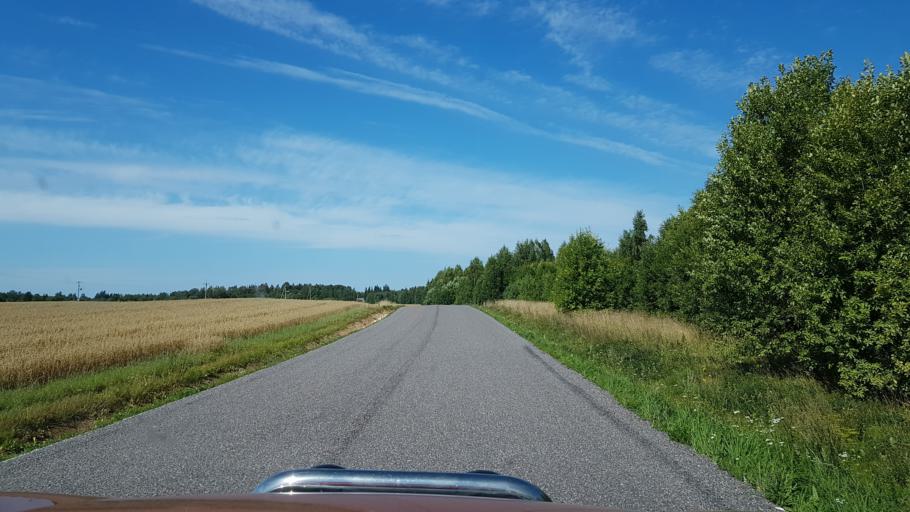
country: EE
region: Tartu
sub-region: Elva linn
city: Elva
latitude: 58.2491
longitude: 26.3407
